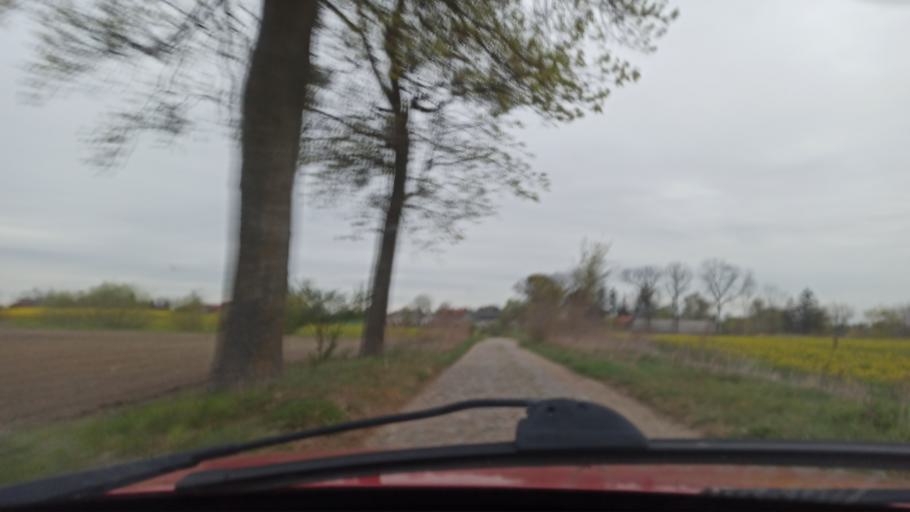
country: PL
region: Kujawsko-Pomorskie
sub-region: Powiat grudziadzki
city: Lasin
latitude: 53.5808
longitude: 19.0930
